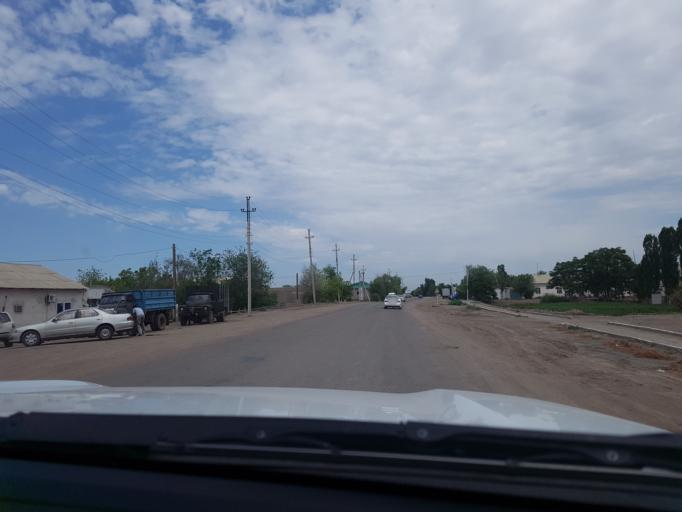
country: TM
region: Dasoguz
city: Koeneuergench
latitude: 42.3129
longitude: 59.1382
